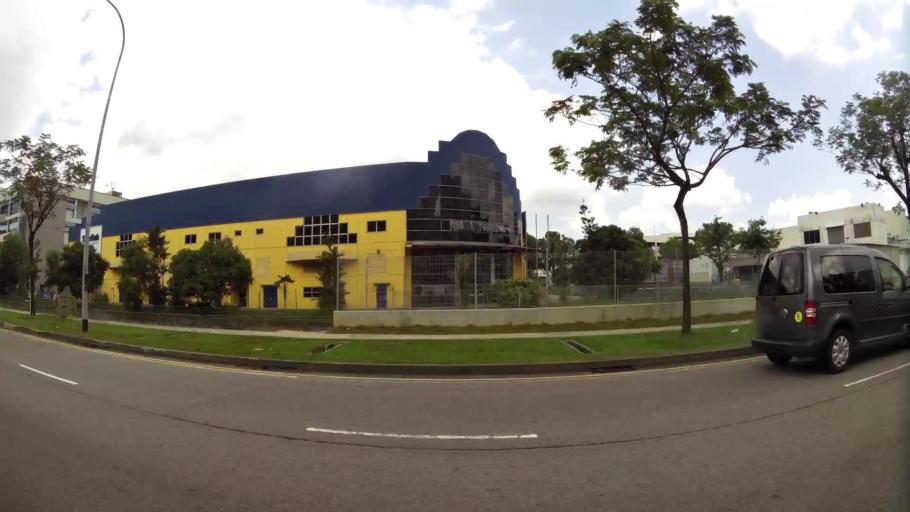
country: MY
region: Johor
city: Johor Bahru
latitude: 1.4467
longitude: 103.8064
